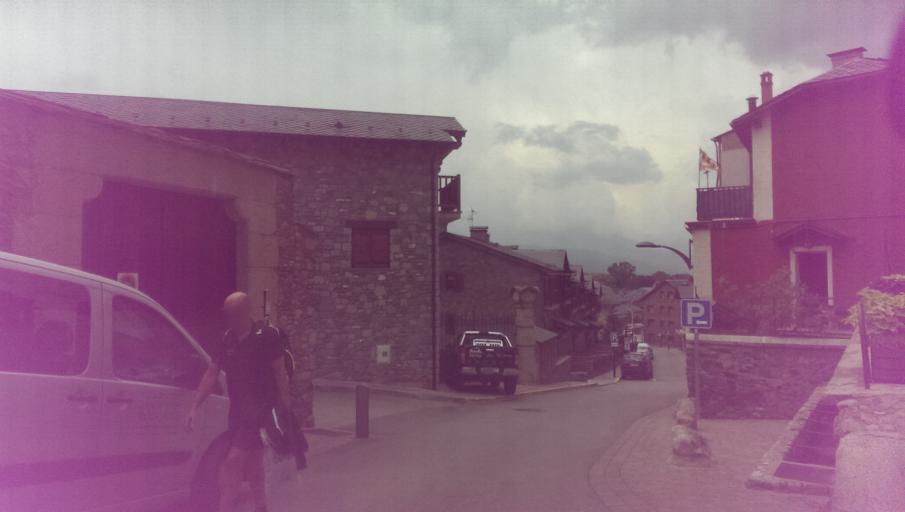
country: ES
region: Catalonia
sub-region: Provincia de Girona
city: Llivia
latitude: 42.4644
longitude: 1.9807
